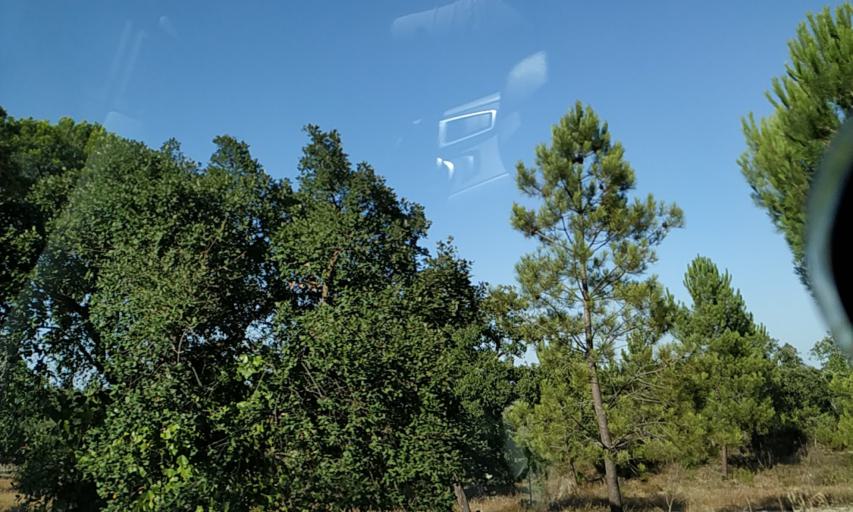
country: PT
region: Santarem
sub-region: Coruche
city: Coruche
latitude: 38.9741
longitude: -8.5391
